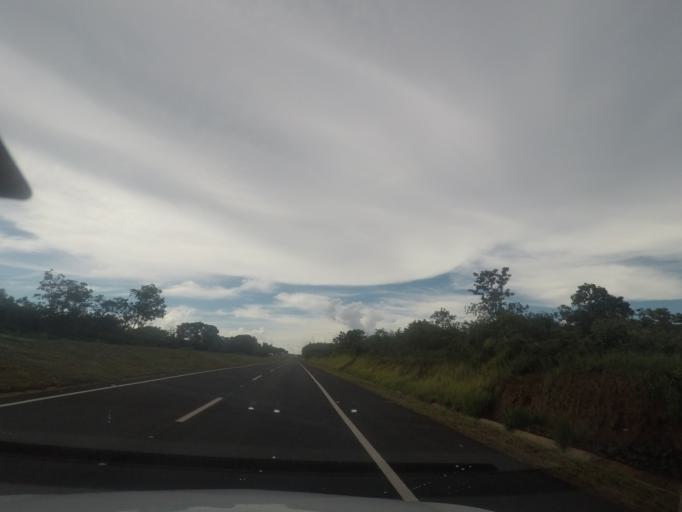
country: BR
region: Minas Gerais
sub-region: Prata
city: Prata
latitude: -19.4059
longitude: -48.8951
